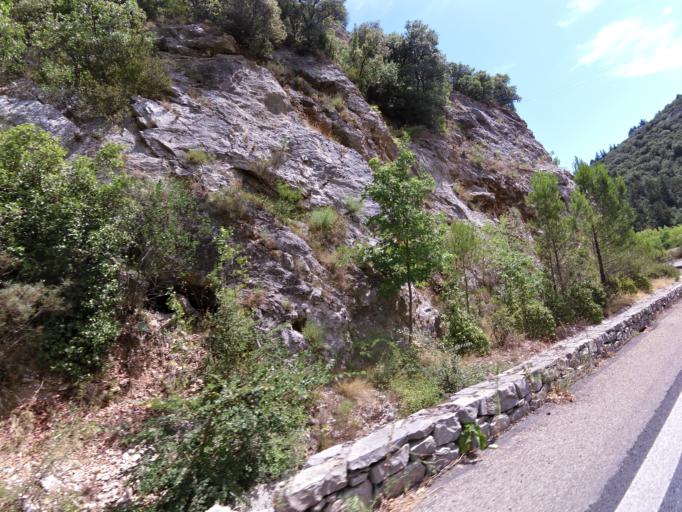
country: FR
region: Languedoc-Roussillon
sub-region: Departement de l'Herault
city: Ganges
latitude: 43.9395
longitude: 3.6904
